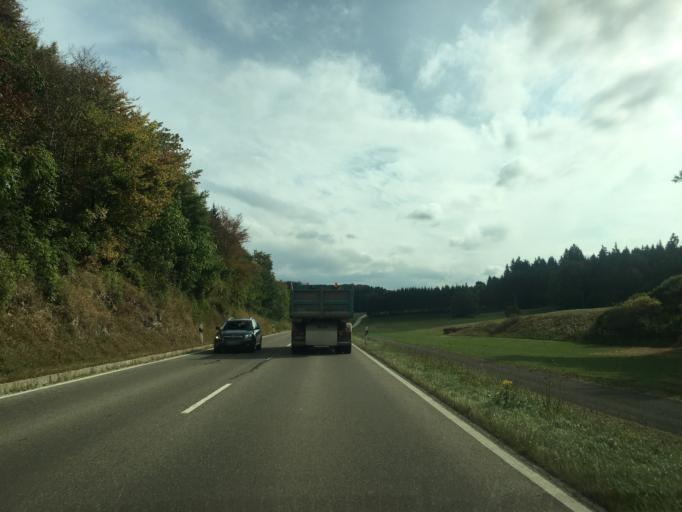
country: DE
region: Baden-Wuerttemberg
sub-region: Tuebingen Region
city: Pfullingen
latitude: 48.4011
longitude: 9.2164
